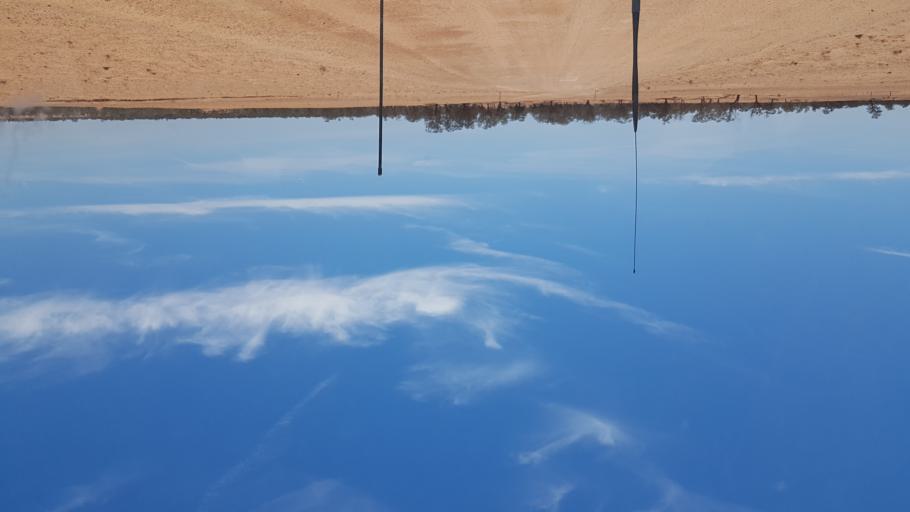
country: AU
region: New South Wales
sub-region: Wentworth
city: Dareton
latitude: -33.3458
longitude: 141.4587
